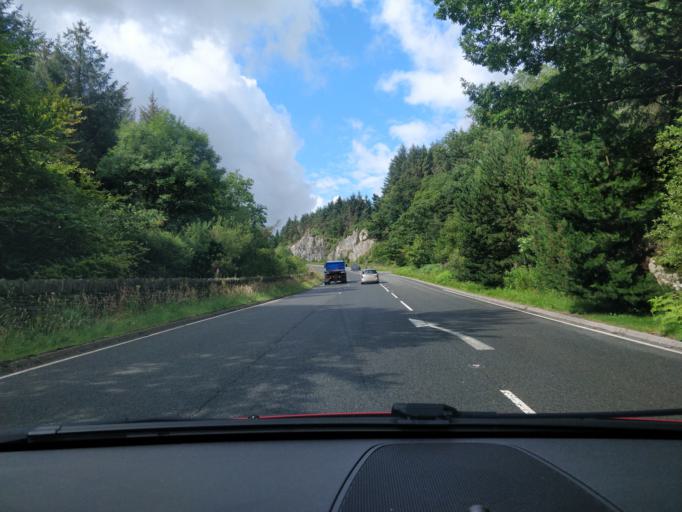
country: GB
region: Wales
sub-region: Gwynedd
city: Blaenau-Ffestiniog
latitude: 53.0415
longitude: -3.9206
